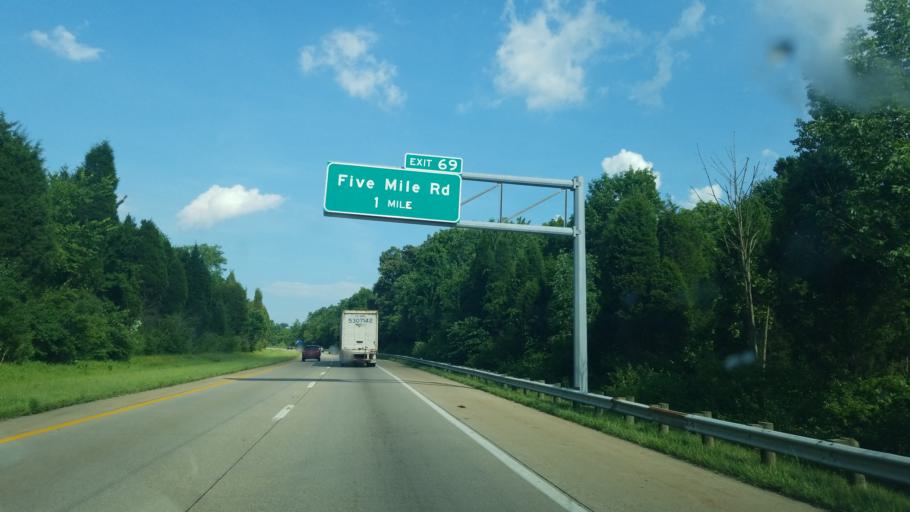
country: US
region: Ohio
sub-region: Hamilton County
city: Salem Heights
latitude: 39.0559
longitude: -84.3782
